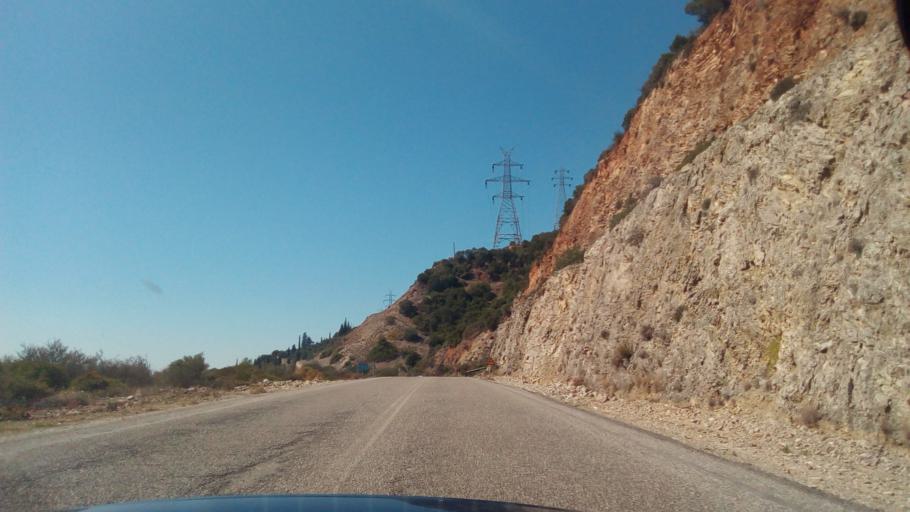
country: GR
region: West Greece
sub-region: Nomos Achaias
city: Kamarai
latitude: 38.3951
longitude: 22.0470
